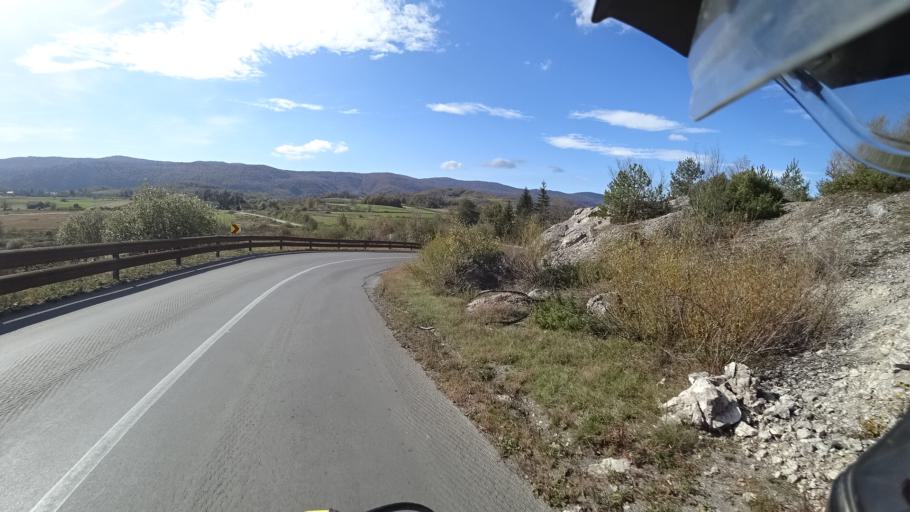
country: HR
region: Karlovacka
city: Plaski
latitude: 45.0986
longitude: 15.3553
